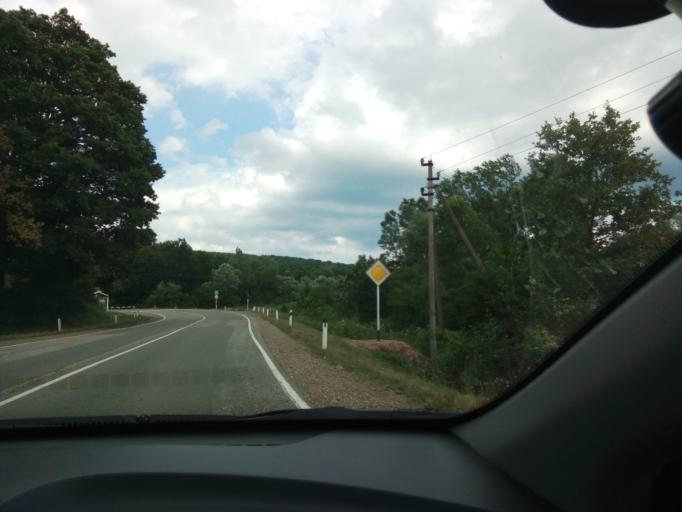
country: RU
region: Krasnodarskiy
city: Apsheronsk
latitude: 44.4439
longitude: 39.8271
